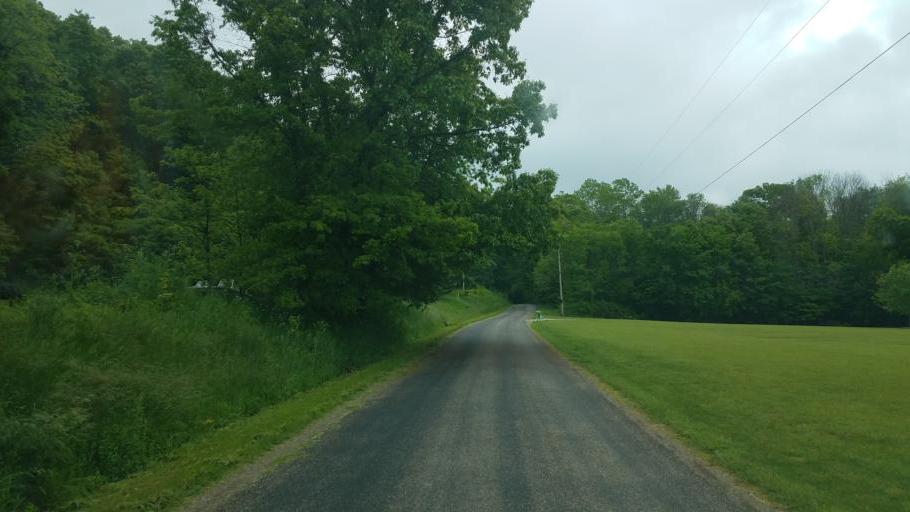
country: US
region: Ohio
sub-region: Richland County
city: Lincoln Heights
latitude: 40.7268
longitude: -82.3584
